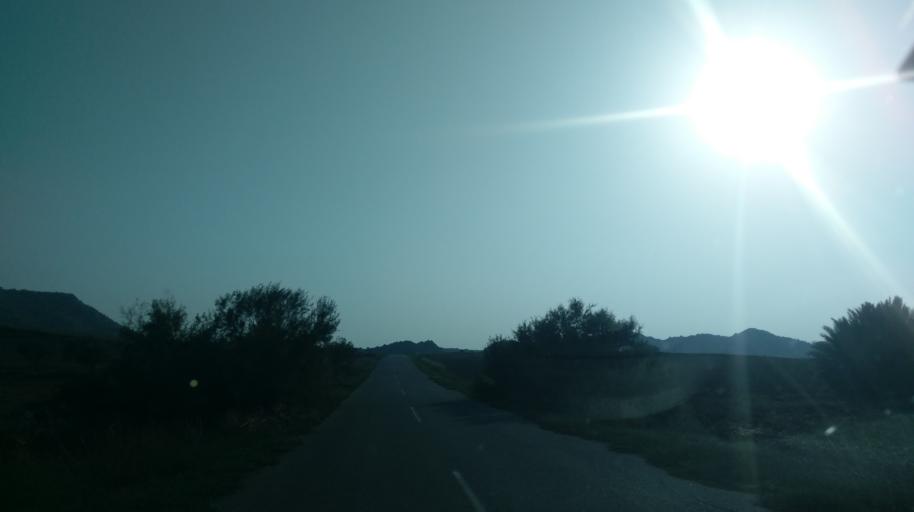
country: CY
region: Ammochostos
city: Leonarisso
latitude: 35.4623
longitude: 34.0980
